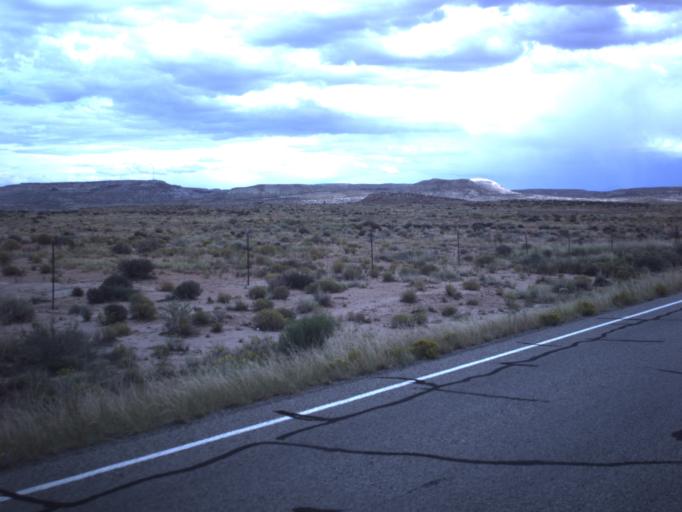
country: US
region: Utah
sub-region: San Juan County
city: Blanding
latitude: 37.2920
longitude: -109.4189
